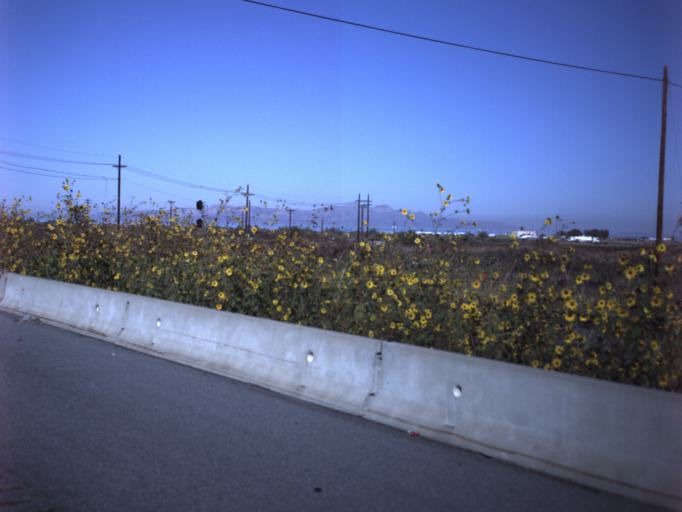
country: US
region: Utah
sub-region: Salt Lake County
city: Magna
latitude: 40.7265
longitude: -112.2004
